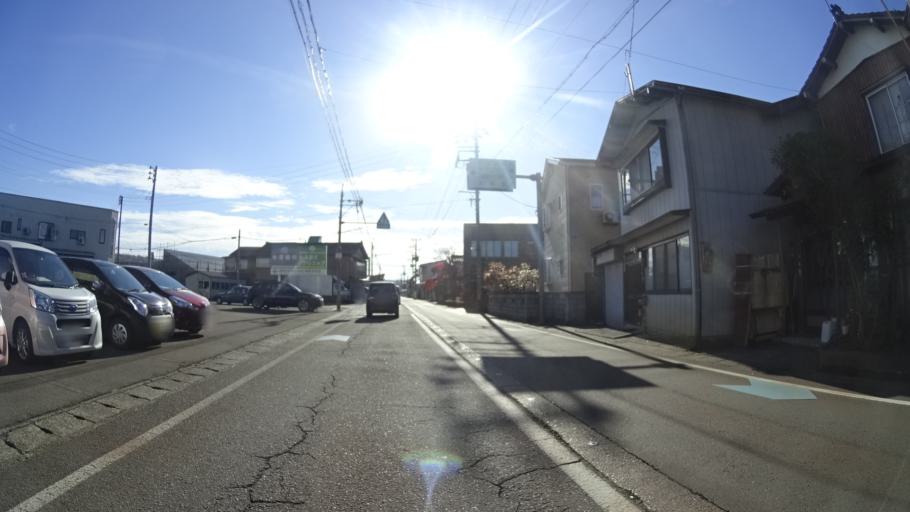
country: JP
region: Niigata
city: Mitsuke
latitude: 37.5340
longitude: 138.9180
